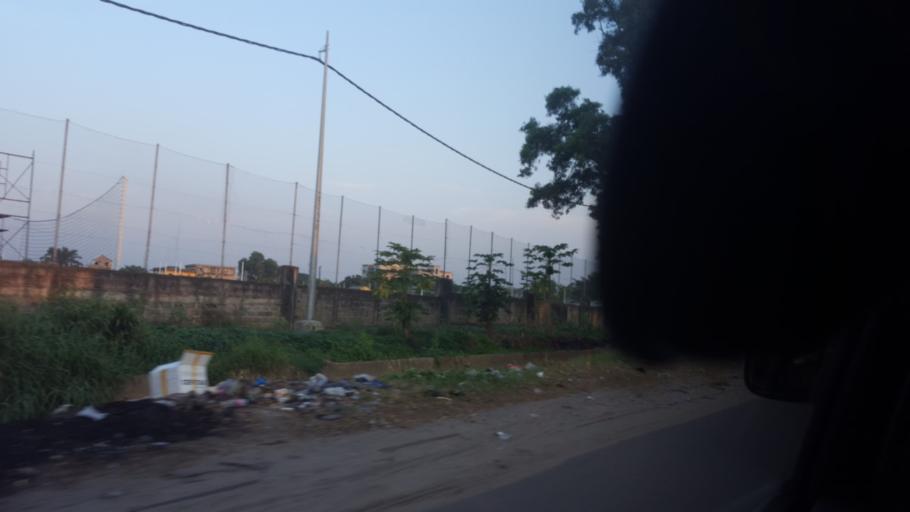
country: CD
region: Kinshasa
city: Kinshasa
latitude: -4.3399
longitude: 15.3204
